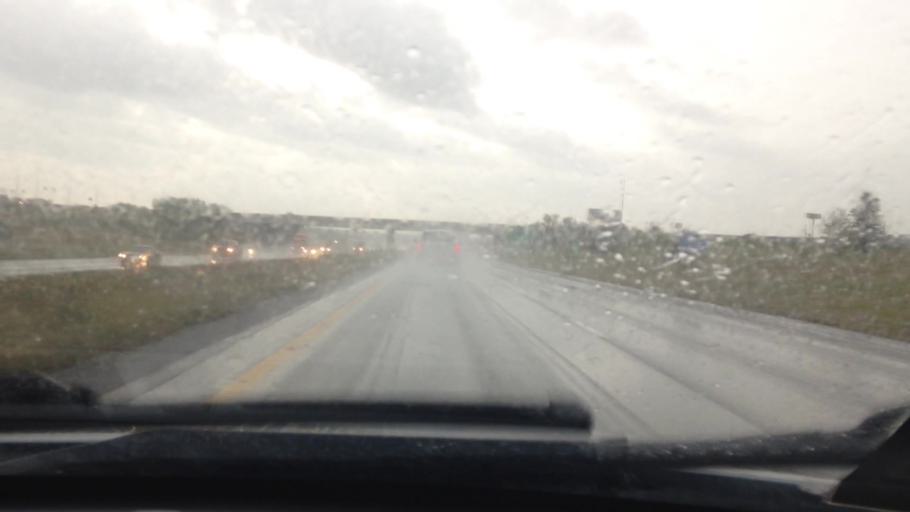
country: US
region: Missouri
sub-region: Platte County
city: Platte City
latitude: 39.3552
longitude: -94.7639
